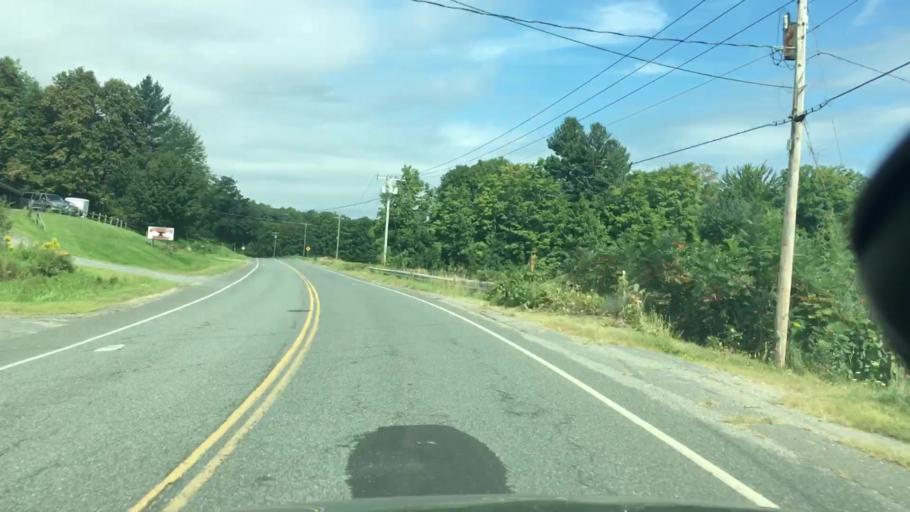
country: US
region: Massachusetts
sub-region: Franklin County
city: Colrain
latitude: 42.6556
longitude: -72.6773
